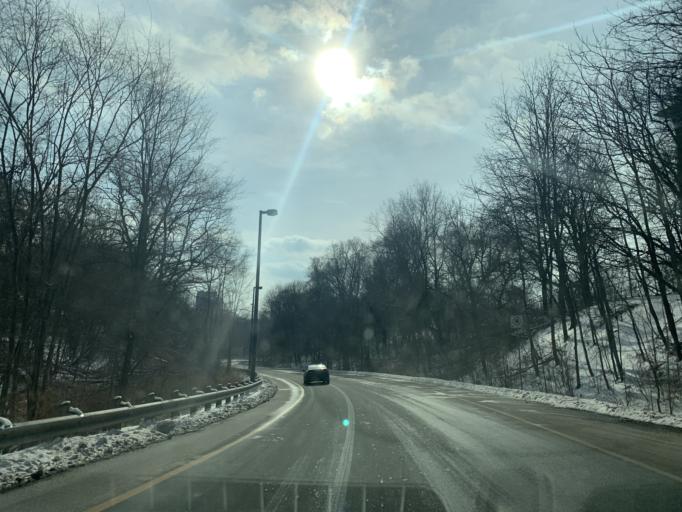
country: CA
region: Ontario
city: Toronto
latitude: 43.6749
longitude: -79.3593
